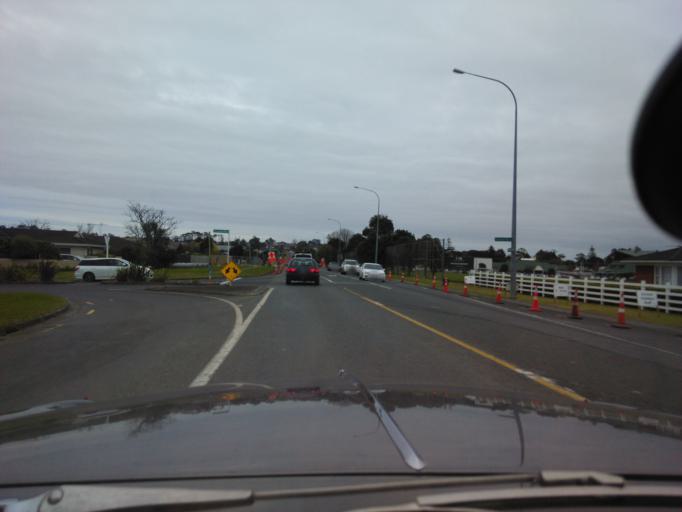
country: NZ
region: Auckland
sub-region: Auckland
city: Rothesay Bay
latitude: -36.7395
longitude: 174.6924
